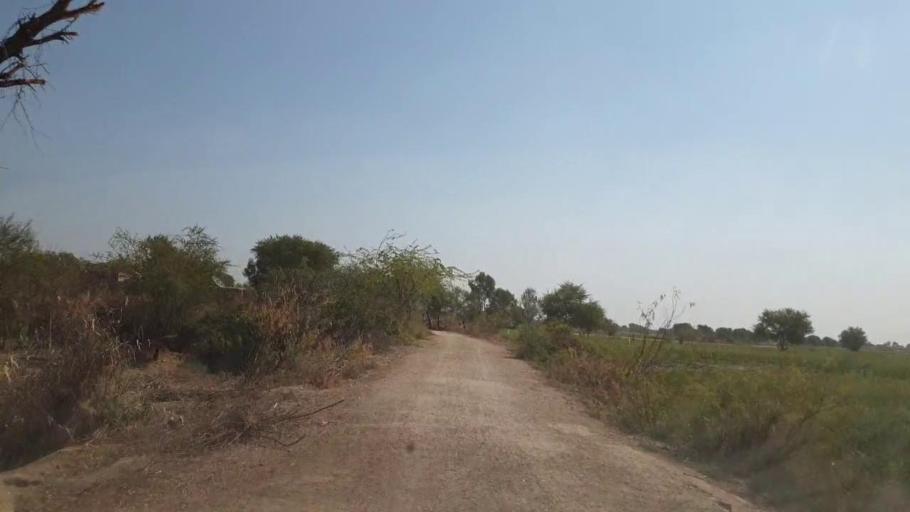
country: PK
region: Sindh
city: Mirpur Khas
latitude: 25.7165
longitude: 69.1022
